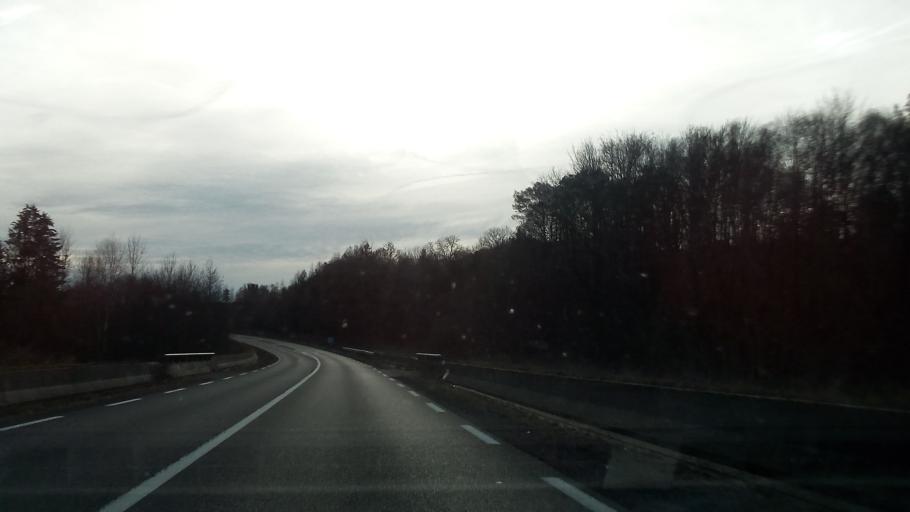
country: FR
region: Limousin
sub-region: Departement de la Correze
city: Seilhac
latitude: 45.3688
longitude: 1.6985
